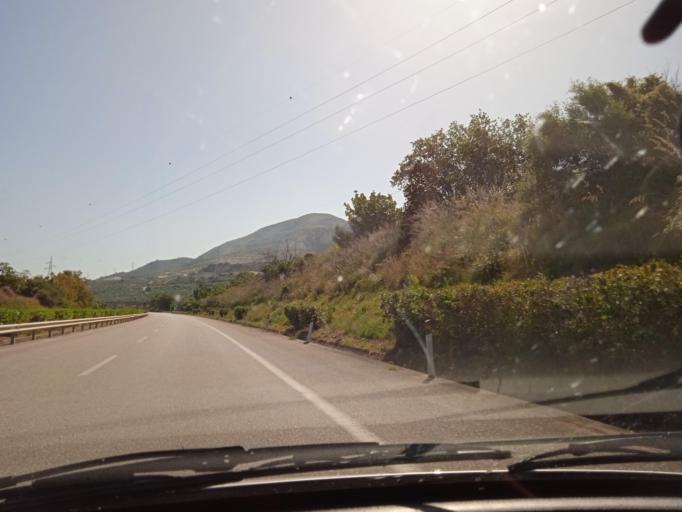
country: IT
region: Sicily
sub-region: Messina
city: Torrenova
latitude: 38.0823
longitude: 14.6822
